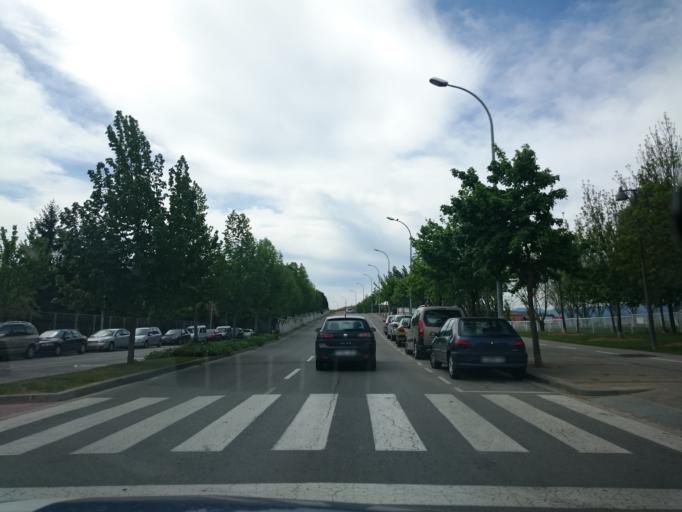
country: ES
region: Catalonia
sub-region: Provincia de Barcelona
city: Vic
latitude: 41.9231
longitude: 2.2487
